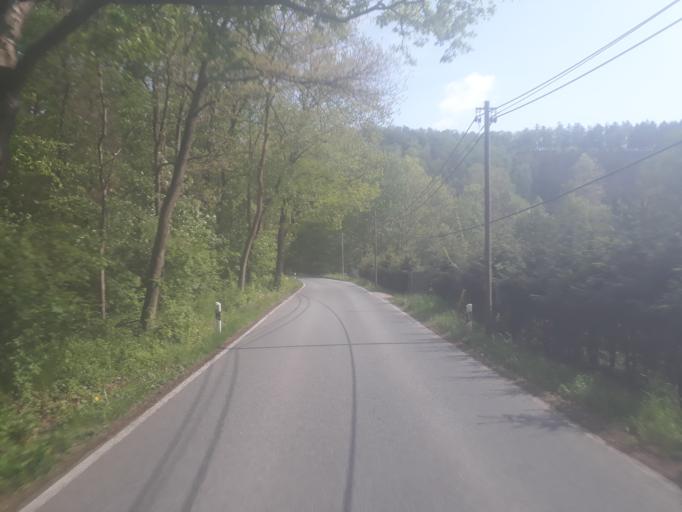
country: DE
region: Saxony
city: Kreischa
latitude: 50.9229
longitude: 13.7786
